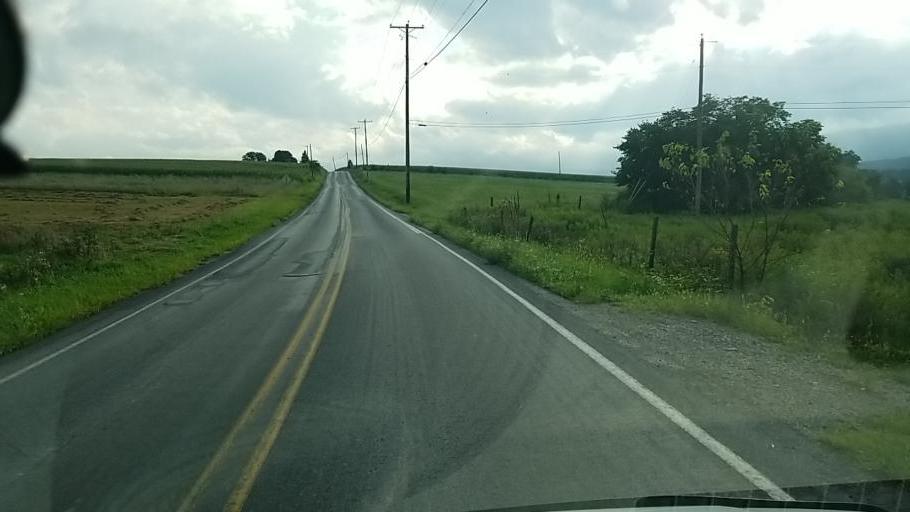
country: US
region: Pennsylvania
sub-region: Cumberland County
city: Shippensburg
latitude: 40.1698
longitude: -77.5556
